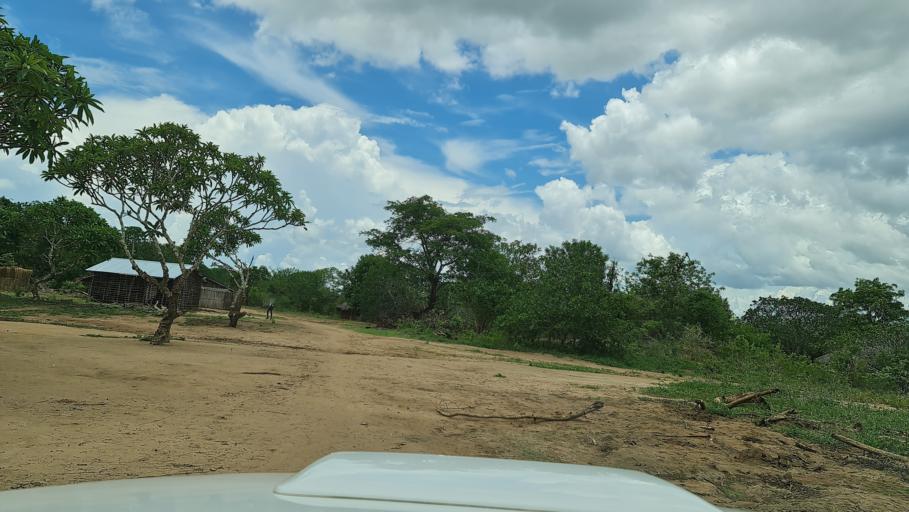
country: MZ
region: Nampula
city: Ilha de Mocambique
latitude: -15.5153
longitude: 40.2029
